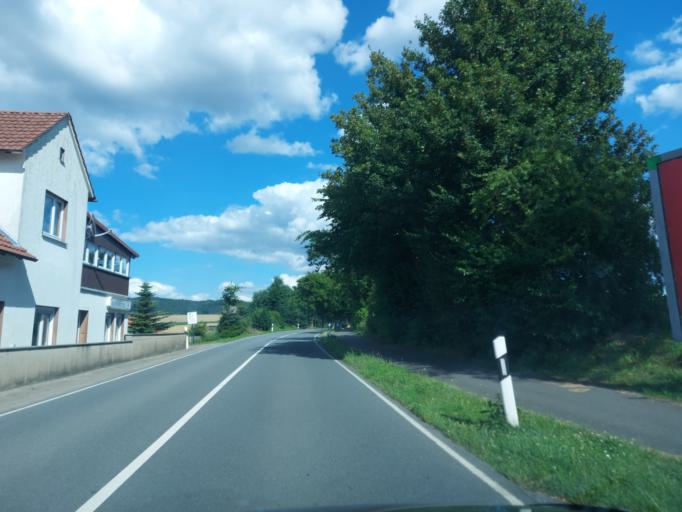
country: DE
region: Lower Saxony
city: Hagen
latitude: 52.1857
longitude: 7.9853
